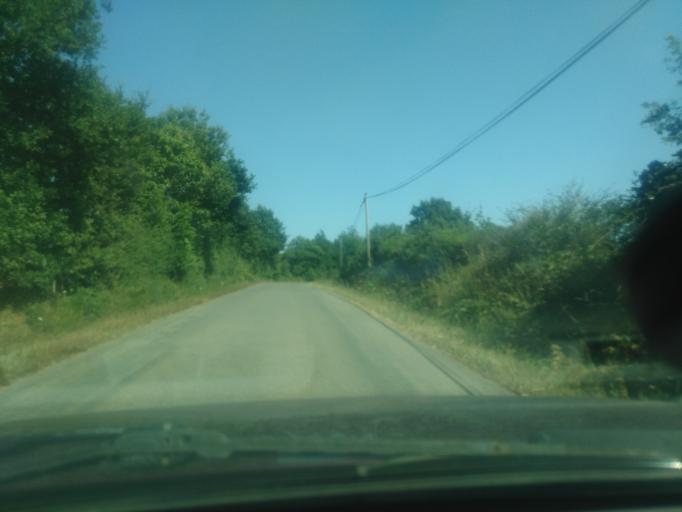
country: FR
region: Pays de la Loire
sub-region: Departement de la Vendee
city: La Ferriere
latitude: 46.7169
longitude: -1.3508
